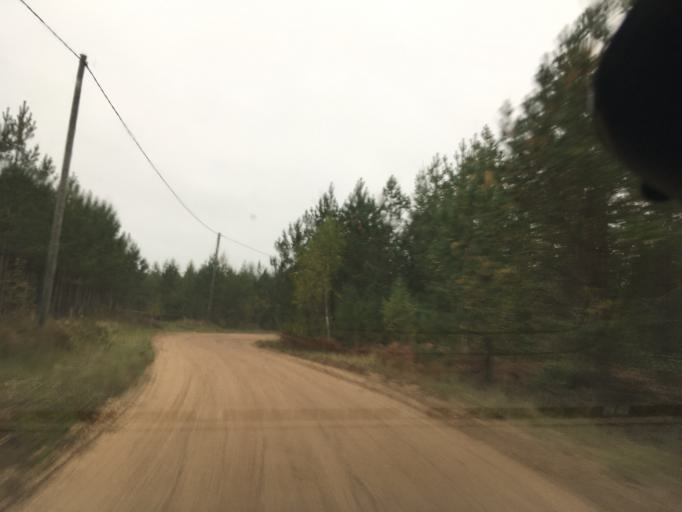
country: LV
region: Kuldigas Rajons
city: Kuldiga
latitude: 57.0204
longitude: 22.0037
